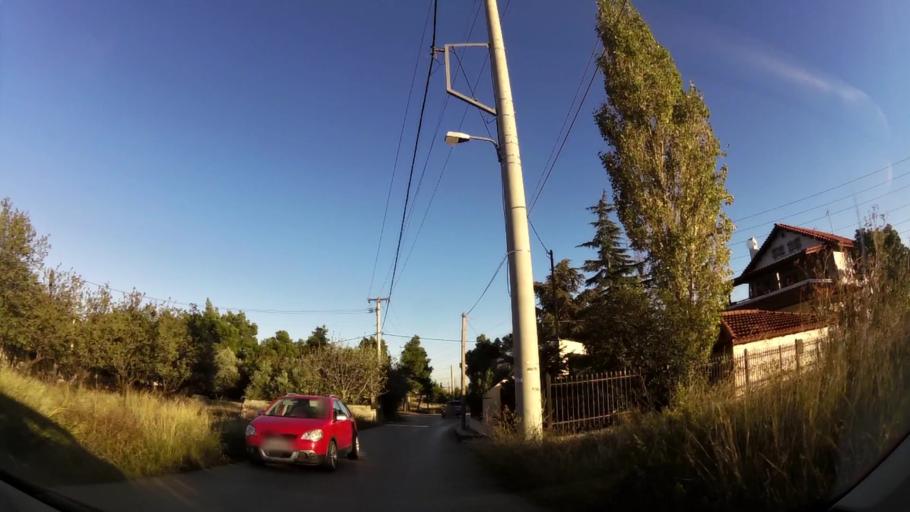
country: GR
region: Attica
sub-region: Nomarchia Anatolikis Attikis
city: Acharnes
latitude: 38.1018
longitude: 23.7194
